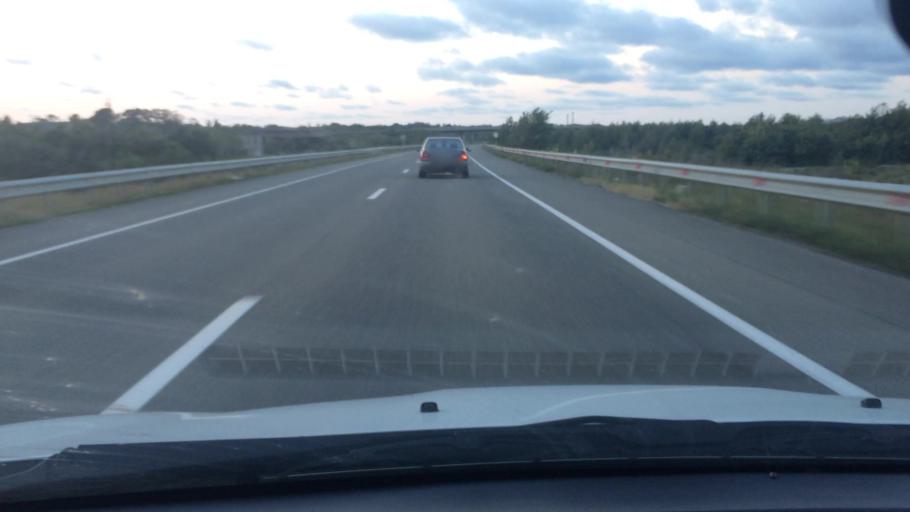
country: GE
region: Guria
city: Urek'i
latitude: 41.9146
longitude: 41.7783
